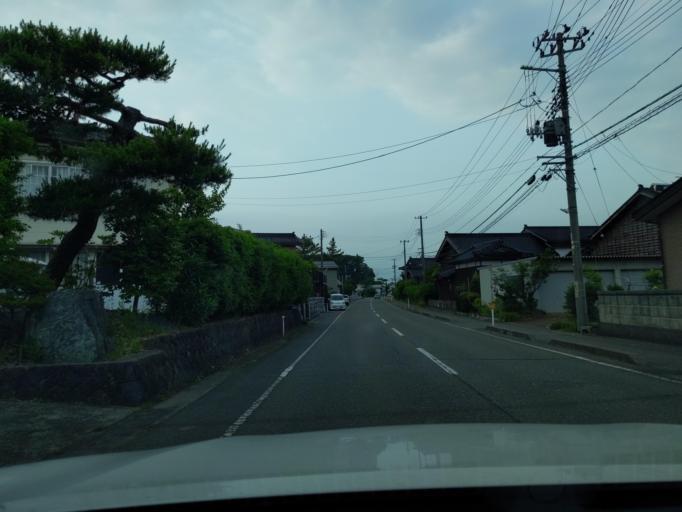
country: JP
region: Niigata
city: Kashiwazaki
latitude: 37.4190
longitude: 138.6152
